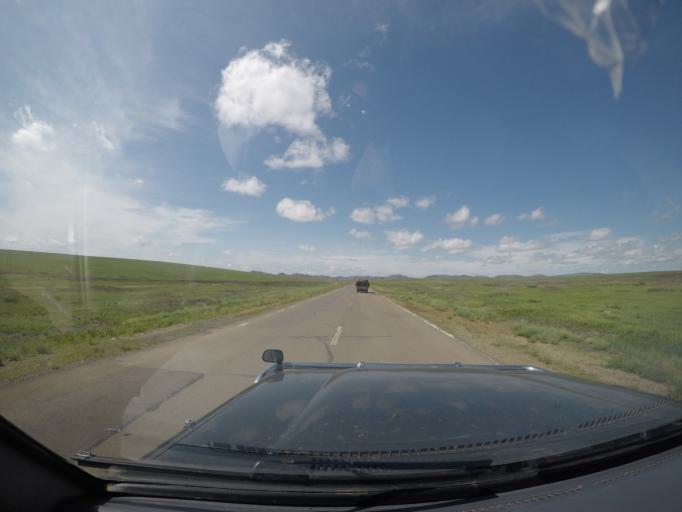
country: MN
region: Hentiy
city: Herlen
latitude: 47.3728
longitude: 110.4808
